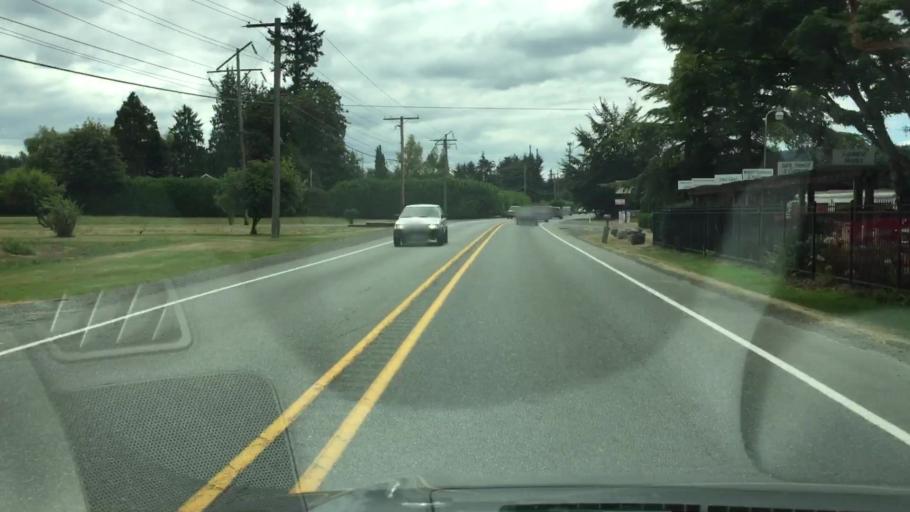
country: US
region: Washington
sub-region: Pierce County
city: Alderton
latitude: 47.1556
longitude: -122.2301
